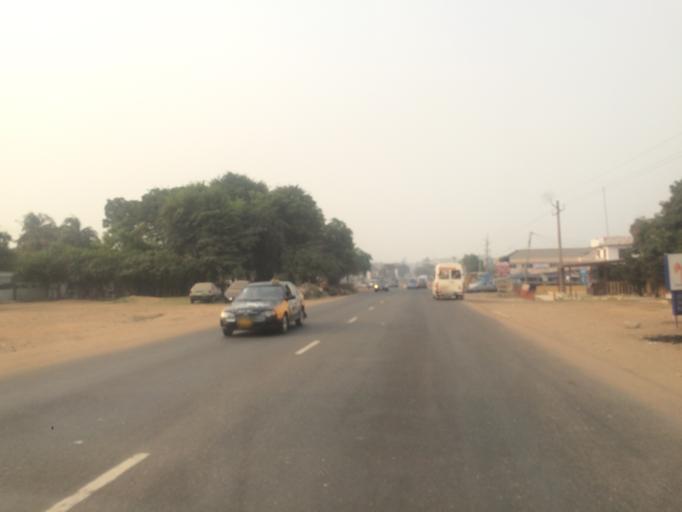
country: GH
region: Greater Accra
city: Nungua
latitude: 5.6116
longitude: -0.0751
